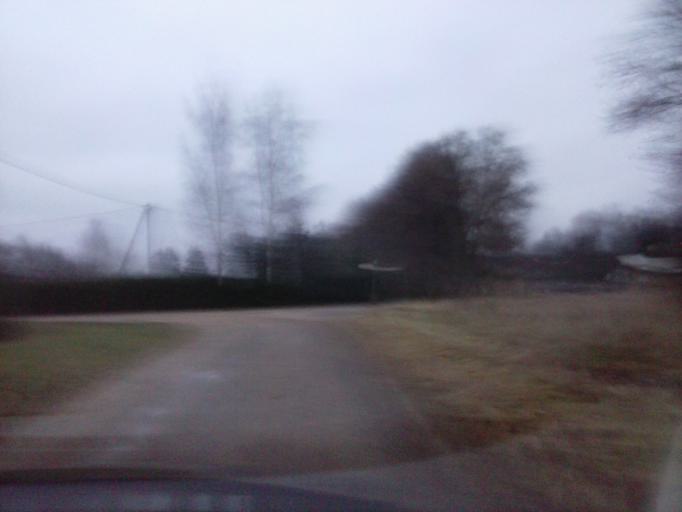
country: EE
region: Tartu
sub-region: Noo vald
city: Noo
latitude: 58.2831
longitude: 26.5433
